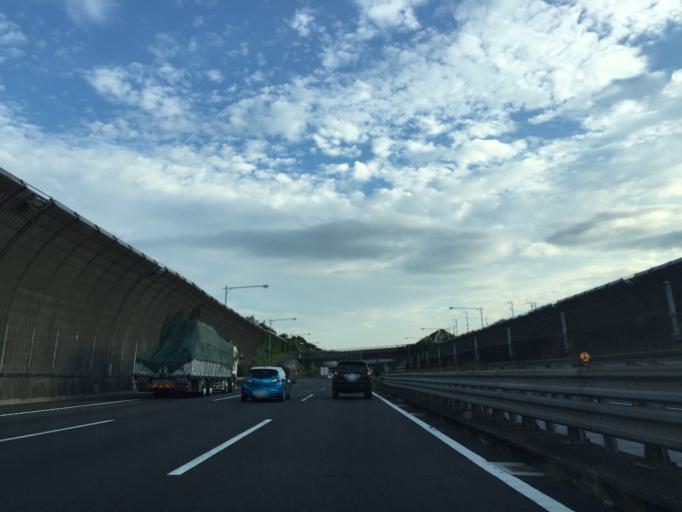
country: JP
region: Kanagawa
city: Hadano
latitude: 35.3733
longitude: 139.2645
